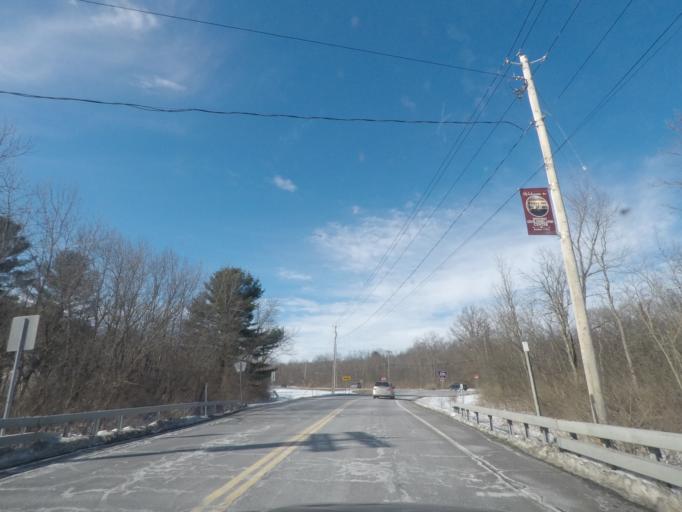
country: US
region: New York
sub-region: Albany County
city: Altamont
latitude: 42.7054
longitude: -73.9762
